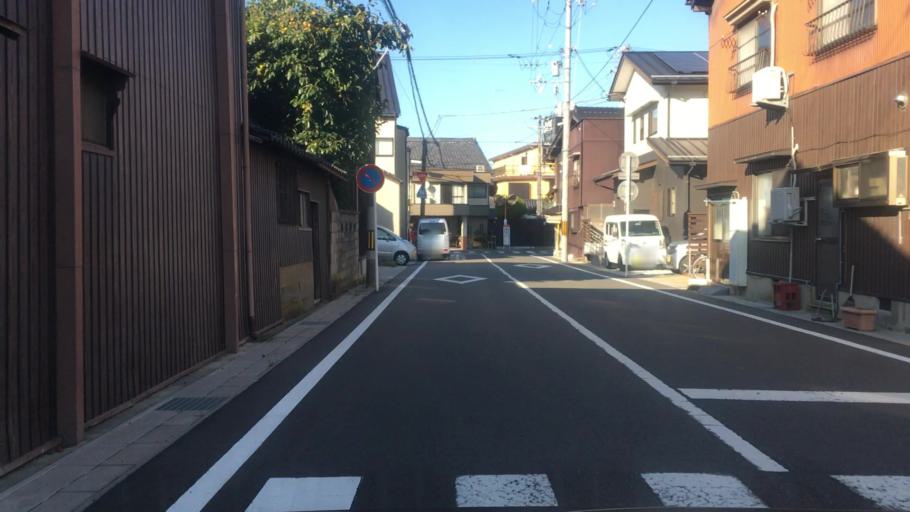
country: JP
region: Hyogo
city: Toyooka
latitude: 35.6067
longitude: 134.8945
